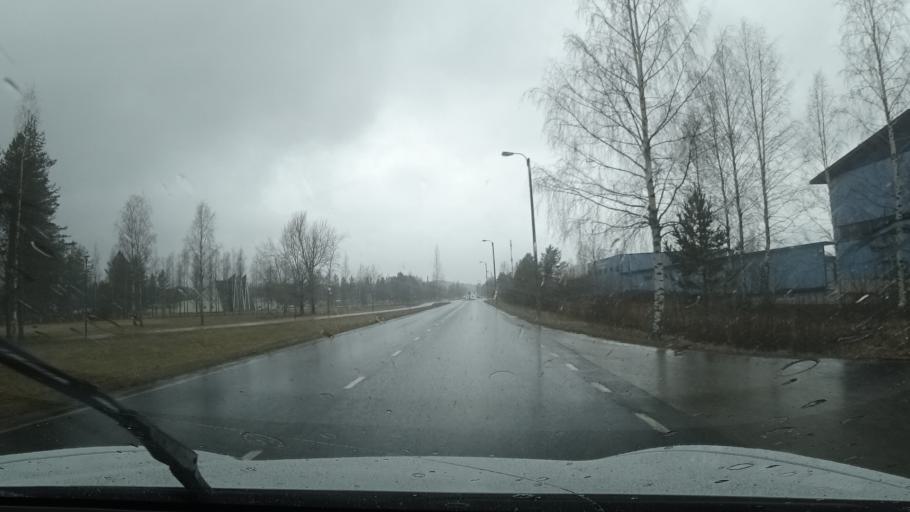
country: FI
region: Paijanne Tavastia
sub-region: Lahti
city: Orimattila
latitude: 60.8024
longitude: 25.7520
